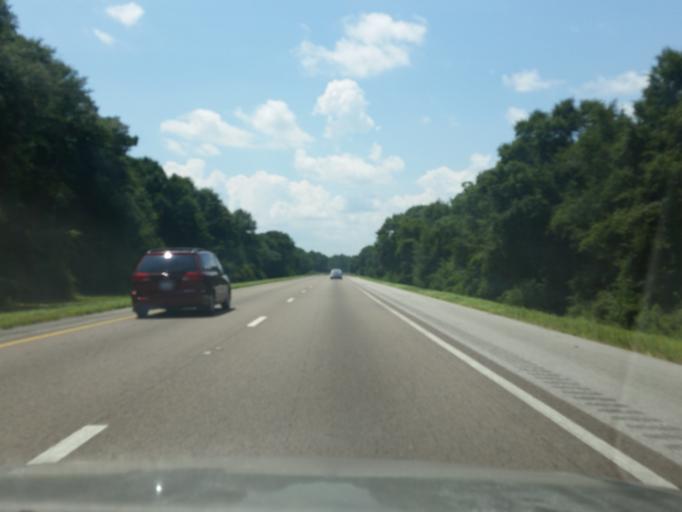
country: US
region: Alabama
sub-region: Baldwin County
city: Robertsdale
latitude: 30.6182
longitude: -87.5827
